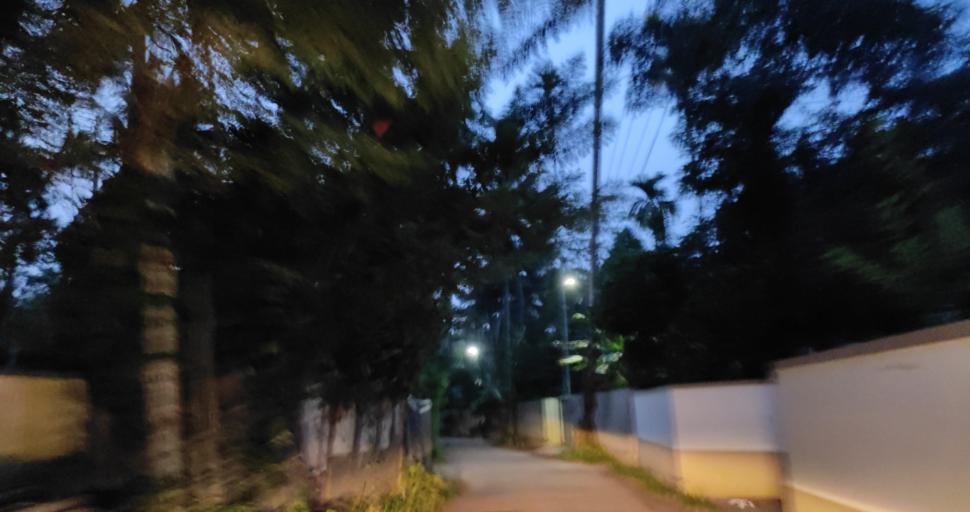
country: IN
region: Kerala
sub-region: Alappuzha
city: Vayalar
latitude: 9.7197
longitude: 76.2916
